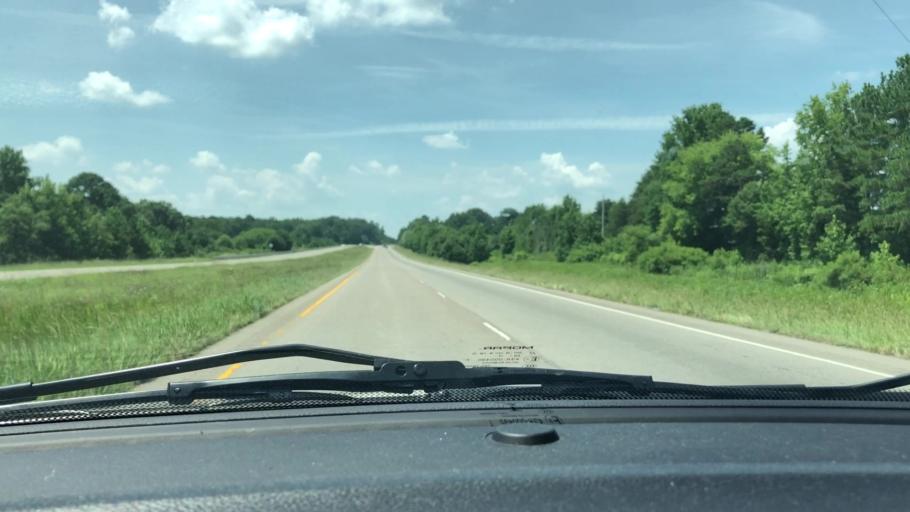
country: US
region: North Carolina
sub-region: Chatham County
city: Siler City
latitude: 35.6219
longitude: -79.3577
